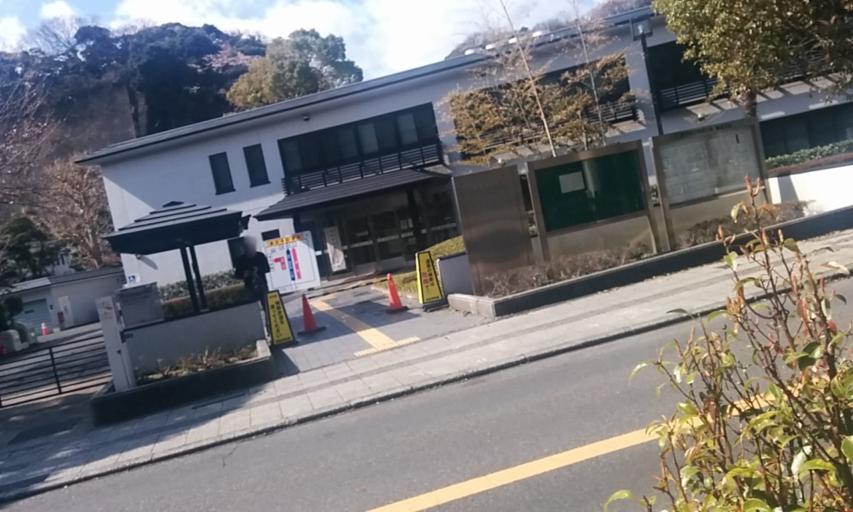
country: JP
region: Kanagawa
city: Kamakura
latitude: 35.3203
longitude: 139.5434
